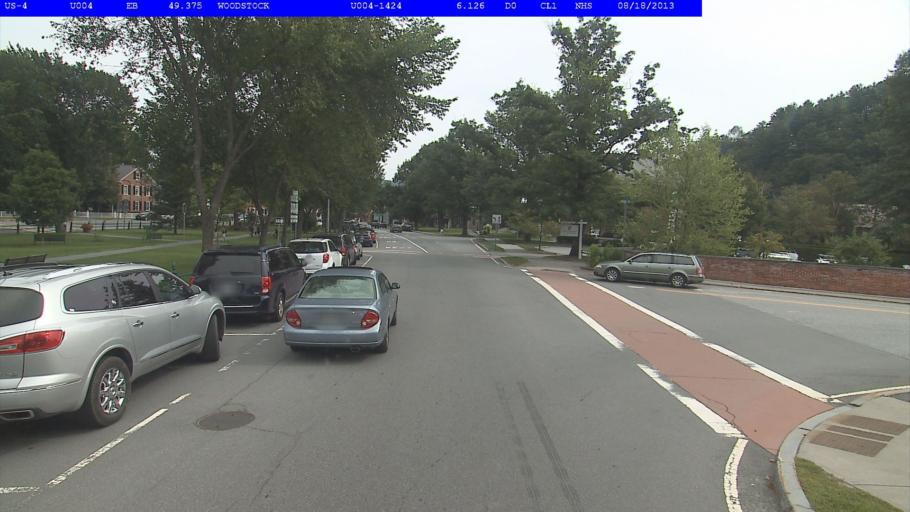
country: US
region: Vermont
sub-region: Windsor County
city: Woodstock
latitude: 43.6237
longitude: -72.5201
